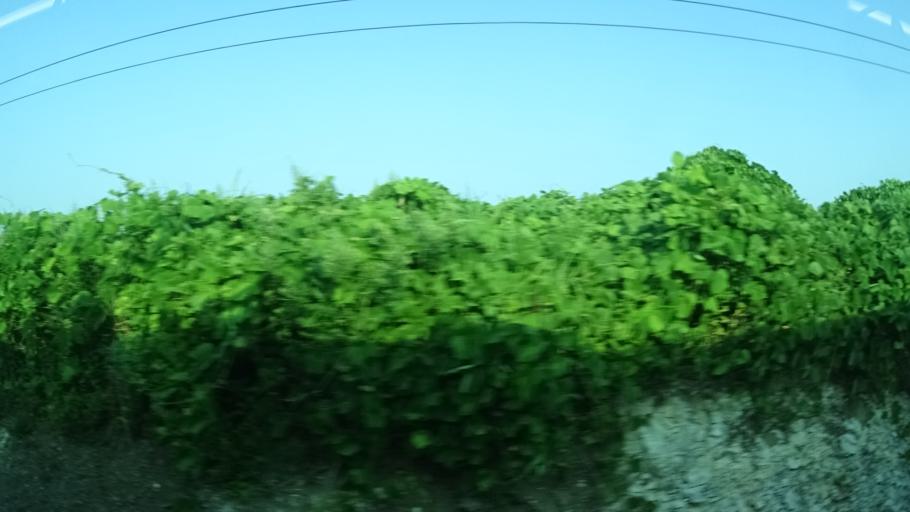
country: JP
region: Ibaraki
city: Takahagi
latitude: 36.7516
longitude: 140.7285
